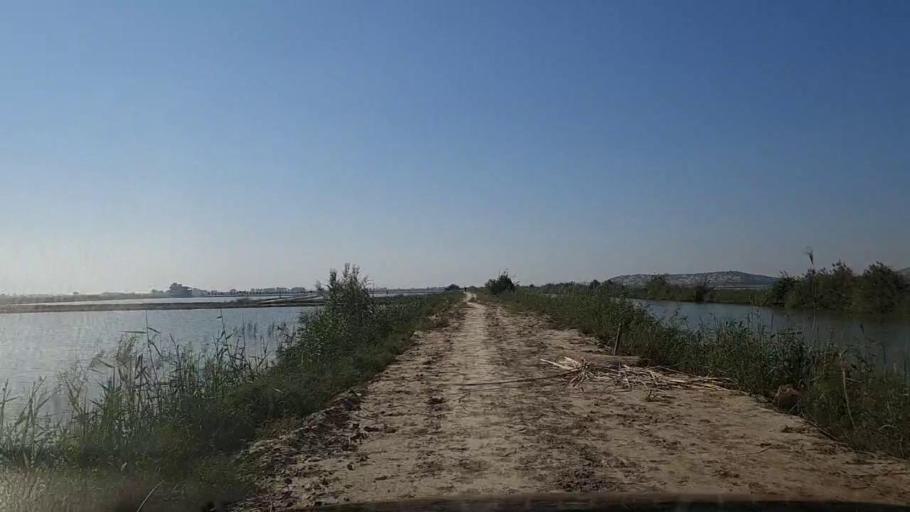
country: PK
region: Sindh
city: Thatta
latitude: 24.6860
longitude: 67.8924
